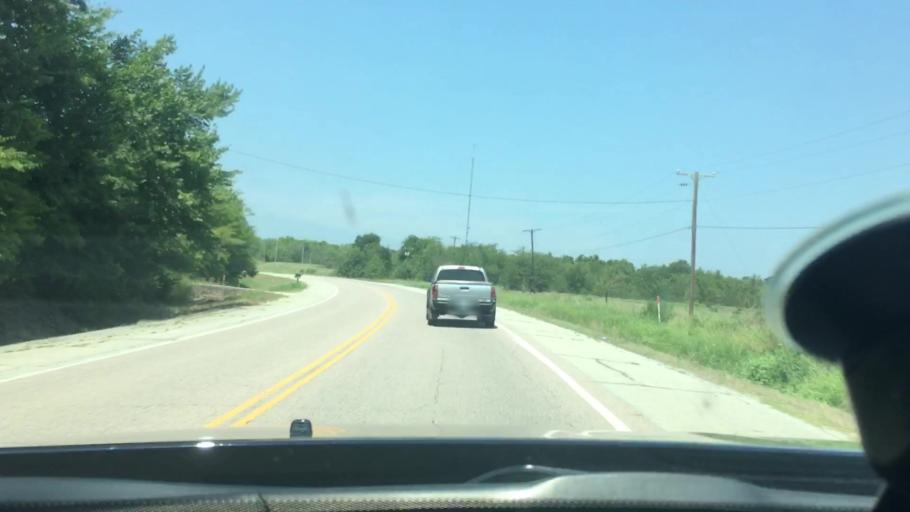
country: US
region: Oklahoma
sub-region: Coal County
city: Coalgate
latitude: 34.5476
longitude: -96.2299
